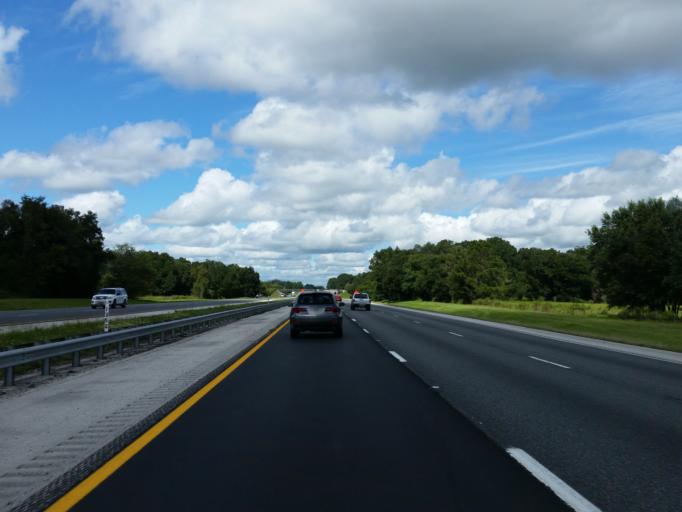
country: US
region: Florida
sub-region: Marion County
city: Ocala
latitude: 29.2895
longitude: -82.2012
